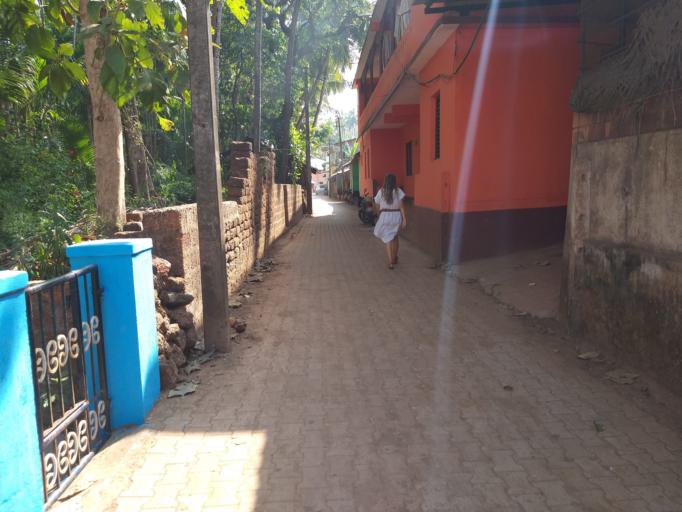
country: IN
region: Karnataka
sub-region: Uttar Kannada
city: Gokarna
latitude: 14.5424
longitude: 74.3176
